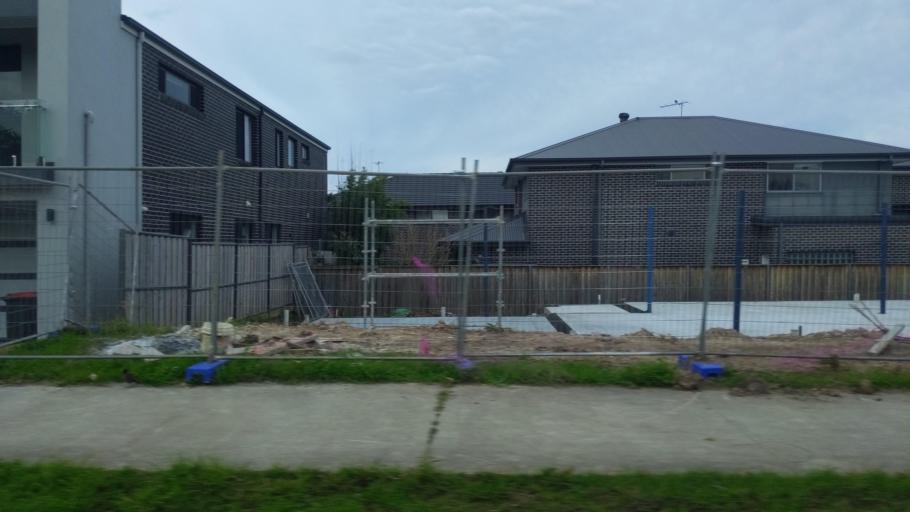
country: AU
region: New South Wales
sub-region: Blacktown
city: Quakers Hill
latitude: -33.7250
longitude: 150.8634
